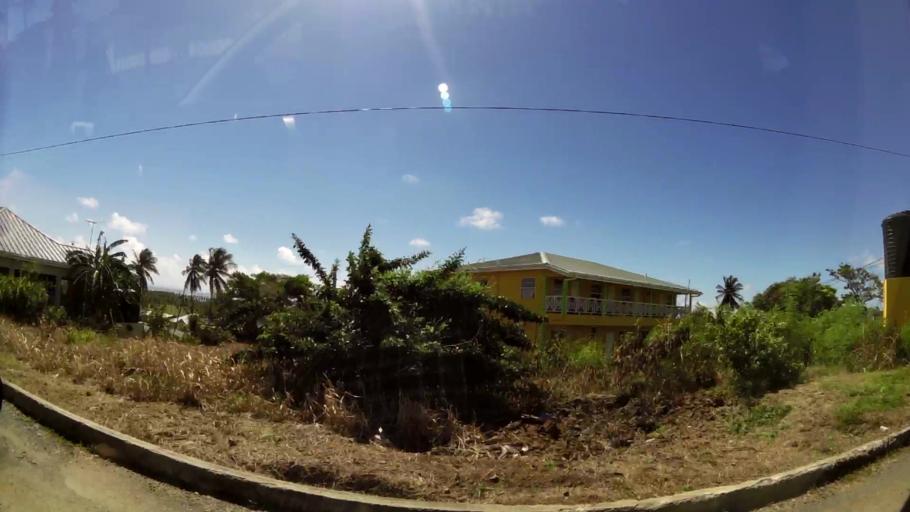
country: TT
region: Tobago
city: Scarborough
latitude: 11.1714
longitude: -60.7763
